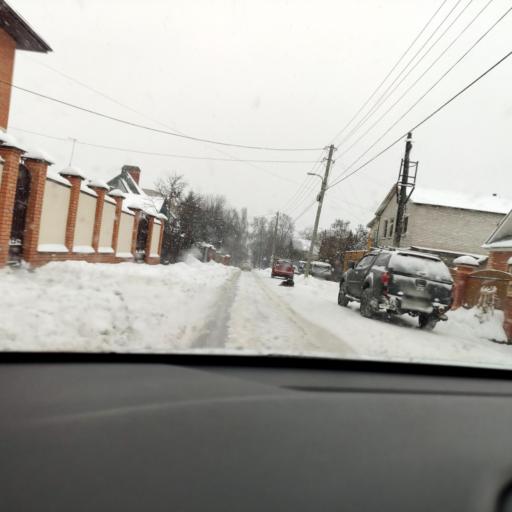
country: RU
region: Tatarstan
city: Vysokaya Gora
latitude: 55.8640
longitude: 49.2326
